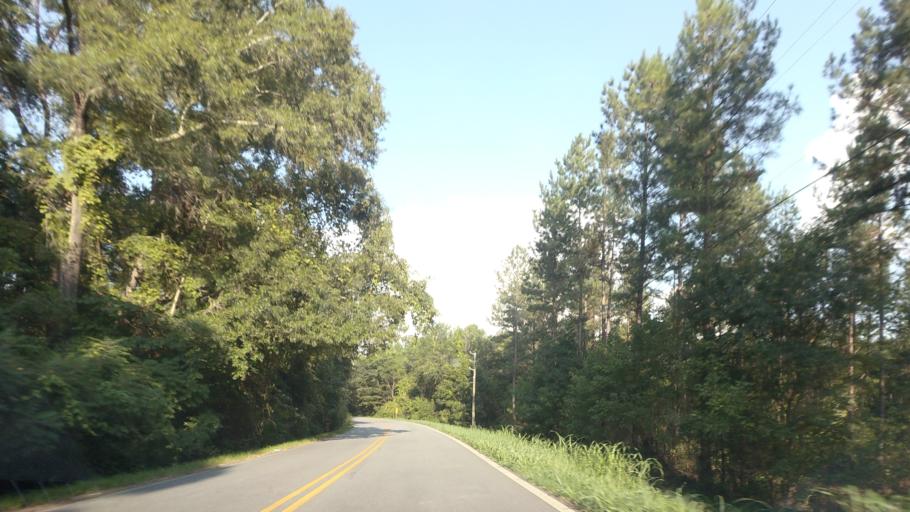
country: US
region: Georgia
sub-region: Bibb County
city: Macon
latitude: 32.8472
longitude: -83.7111
